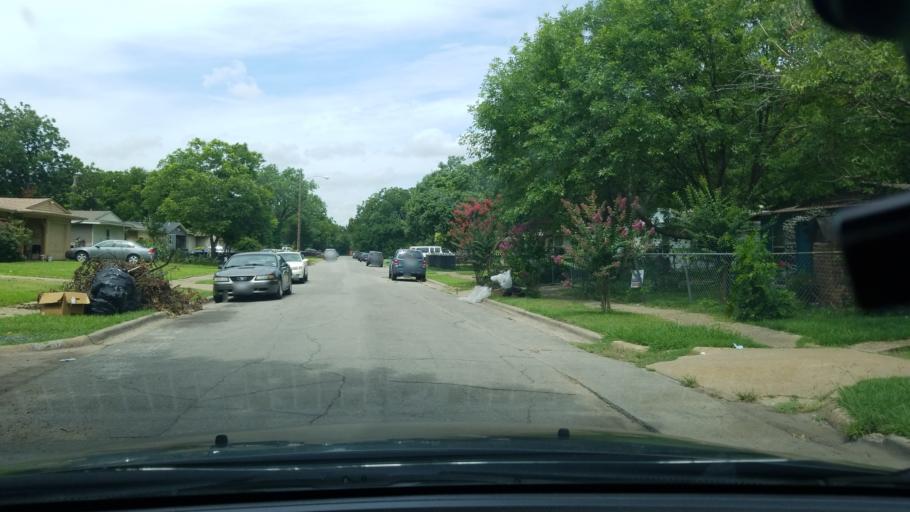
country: US
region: Texas
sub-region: Dallas County
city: Mesquite
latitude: 32.8124
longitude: -96.6738
